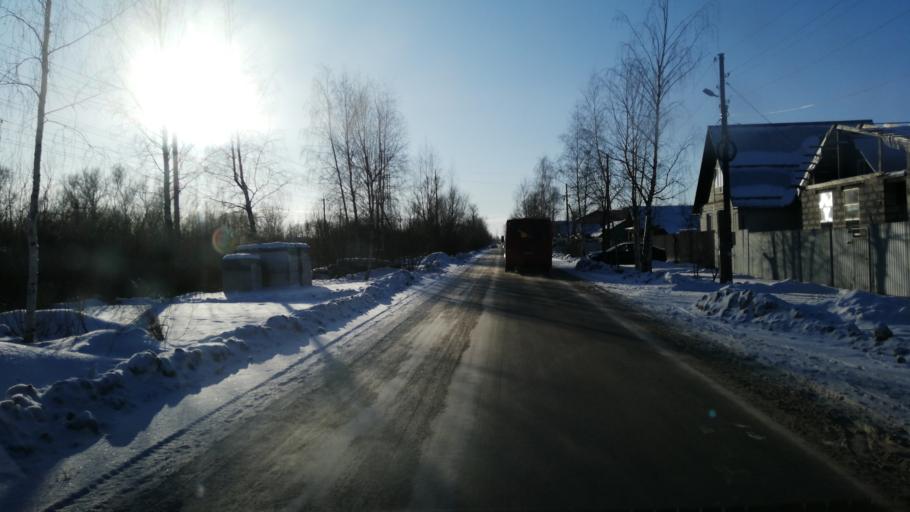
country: RU
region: Jaroslavl
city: Yaroslavl
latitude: 57.6190
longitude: 39.8067
